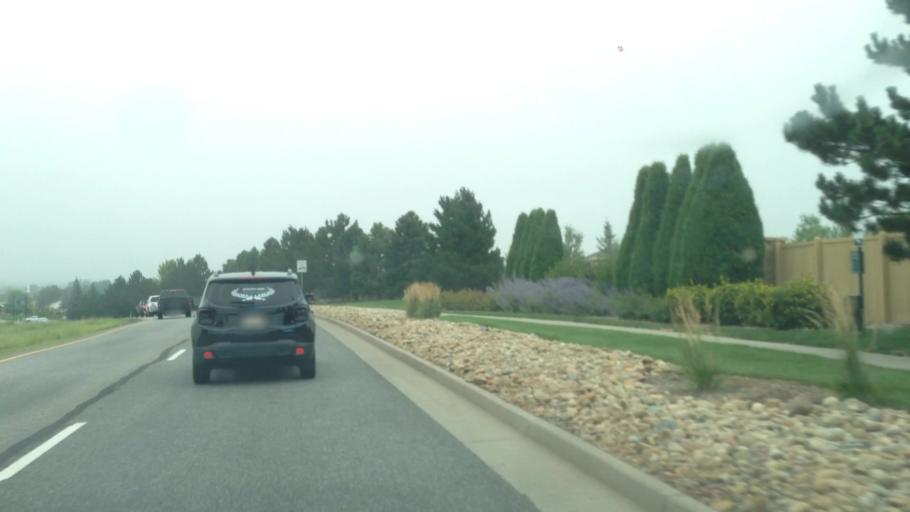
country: US
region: Colorado
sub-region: Douglas County
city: Parker
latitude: 39.6037
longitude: -104.7270
